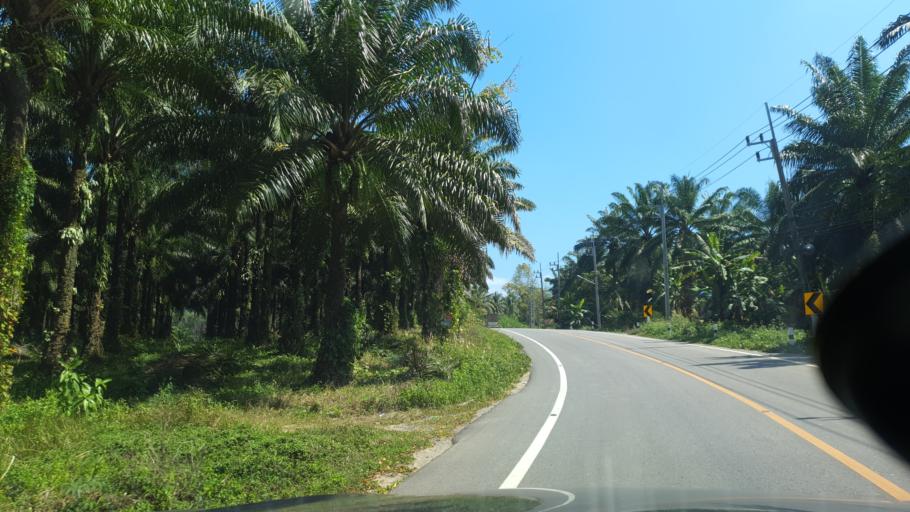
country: TH
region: Krabi
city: Khlong Thom
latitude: 7.9289
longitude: 99.2323
